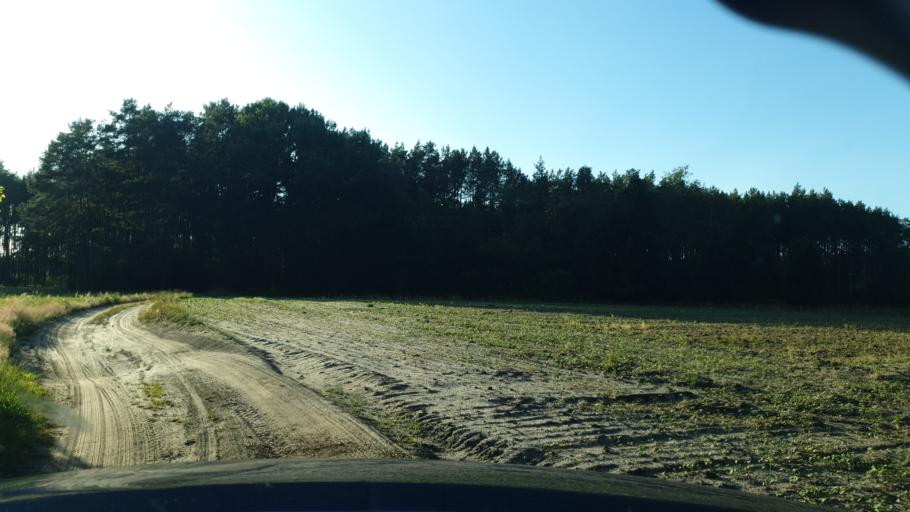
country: PL
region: Pomeranian Voivodeship
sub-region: Powiat bytowski
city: Lipnica
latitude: 53.8870
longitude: 17.4262
